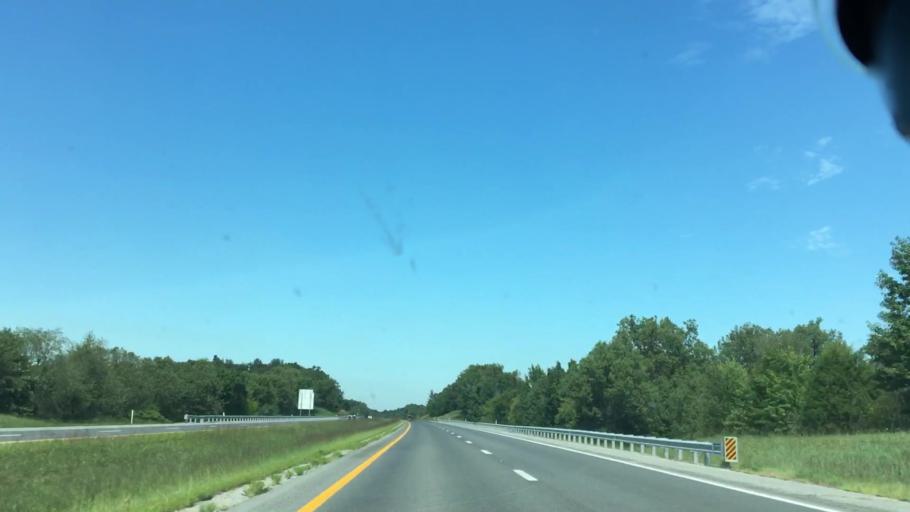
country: US
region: Kentucky
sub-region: Webster County
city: Sebree
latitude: 37.5157
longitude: -87.4747
